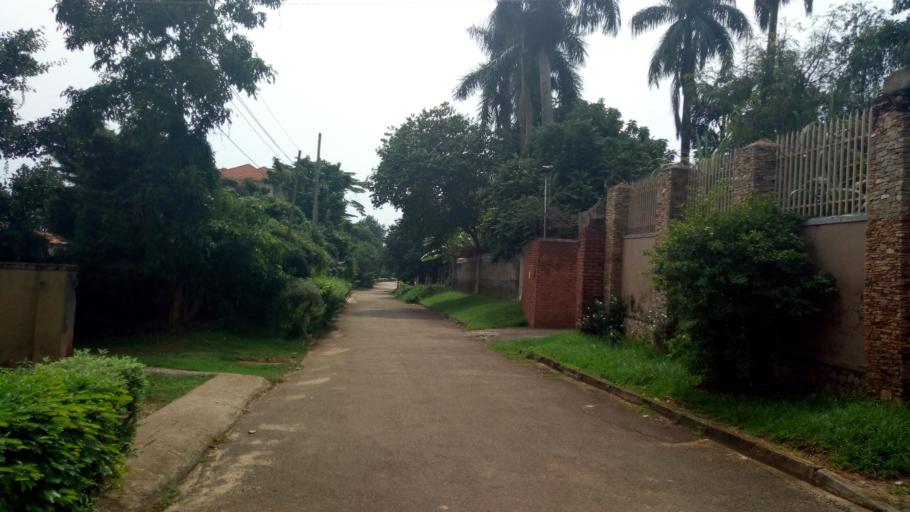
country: UG
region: Central Region
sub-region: Kampala District
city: Kampala
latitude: 0.3112
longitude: 32.6223
